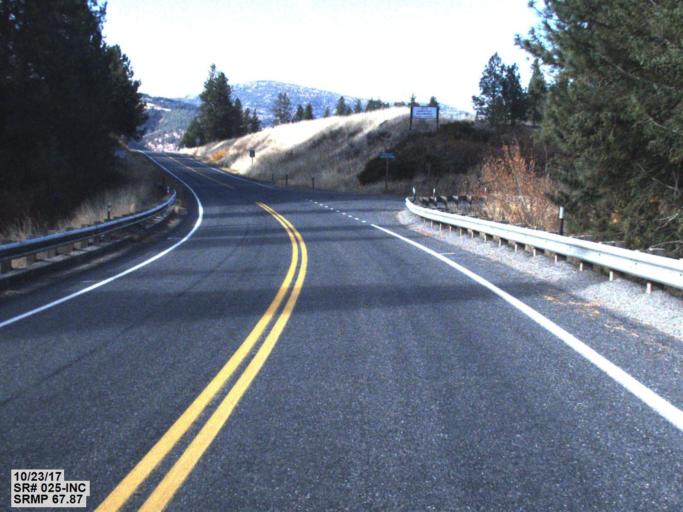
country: US
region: Washington
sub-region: Stevens County
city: Kettle Falls
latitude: 48.4508
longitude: -118.1727
